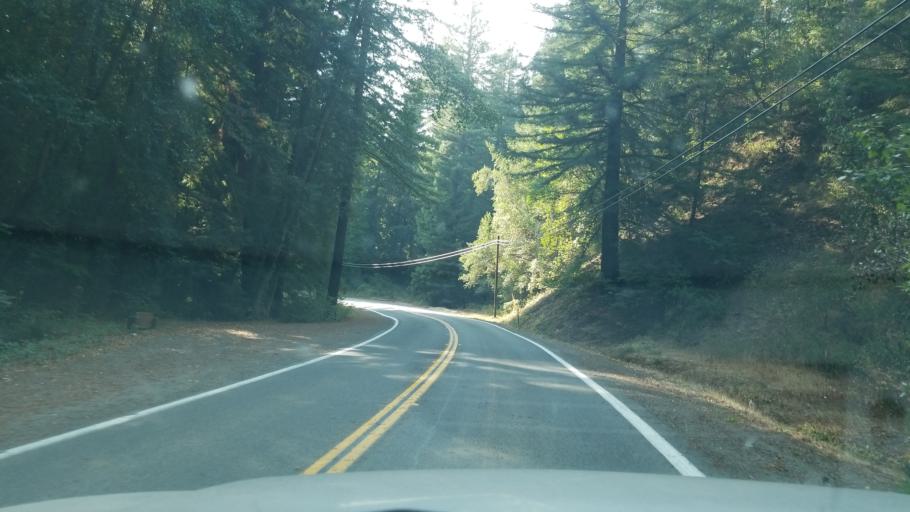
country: US
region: California
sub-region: Humboldt County
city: Redway
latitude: 40.2234
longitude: -123.8023
